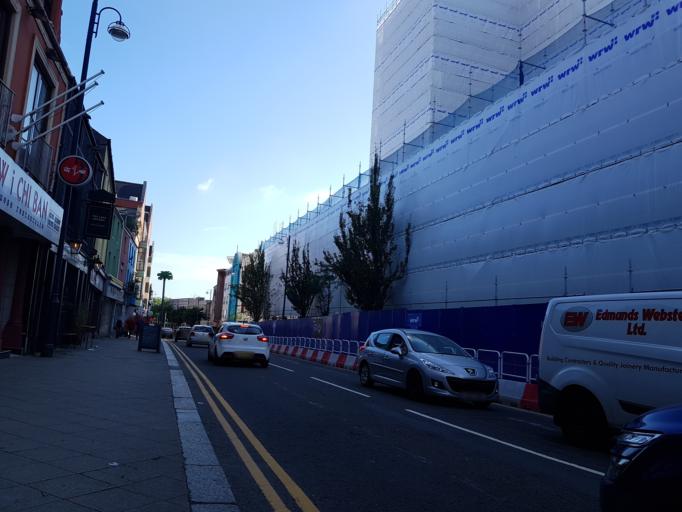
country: GB
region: Wales
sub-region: City and County of Swansea
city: Swansea
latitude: 51.6245
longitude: -3.9418
